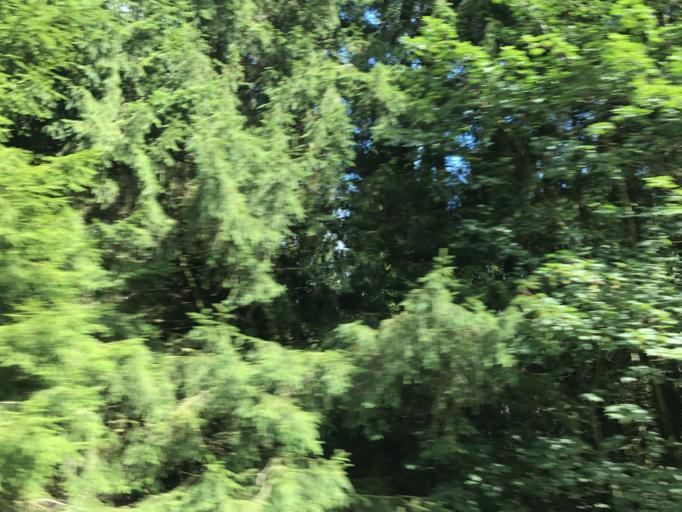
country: DE
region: Lower Saxony
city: Sankt Andreasberg
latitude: 51.7272
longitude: 10.5221
